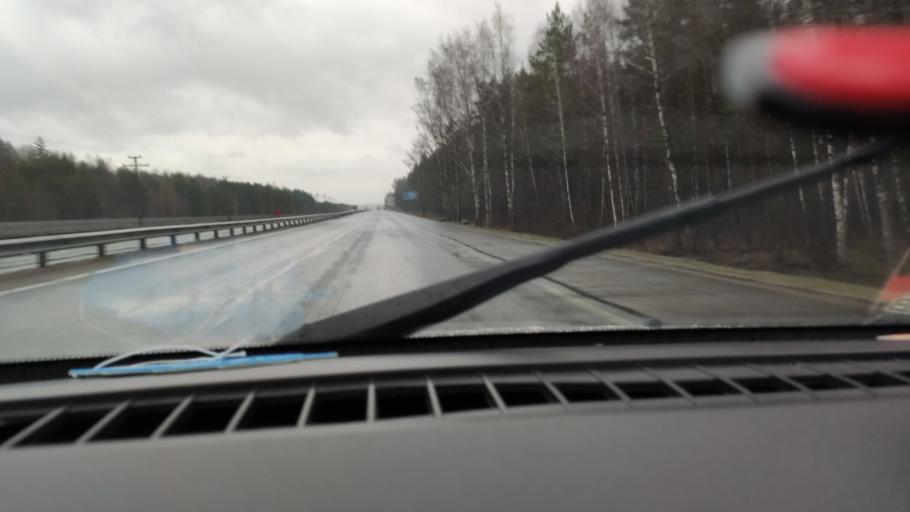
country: RU
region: Tatarstan
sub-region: Tukayevskiy Rayon
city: Naberezhnyye Chelny
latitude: 55.7375
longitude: 52.2506
